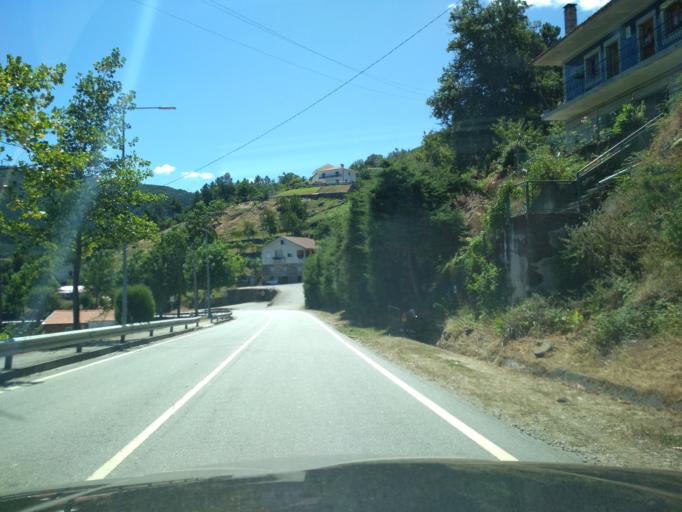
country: PT
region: Vila Real
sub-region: Ribeira de Pena
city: Ribeira de Pena
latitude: 41.5183
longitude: -7.8004
